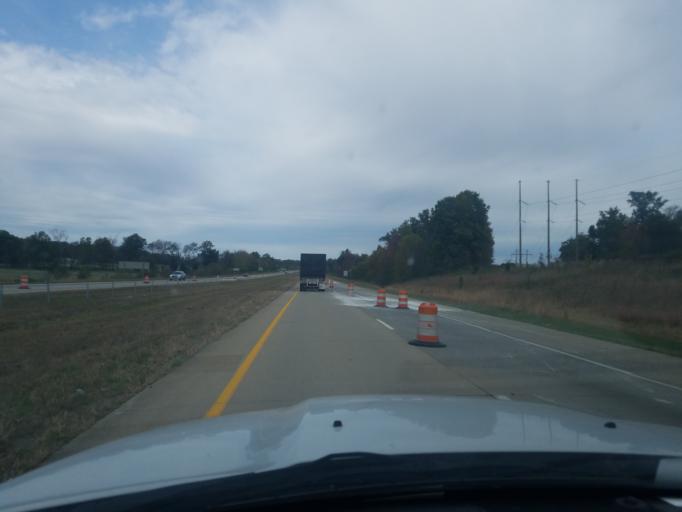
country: US
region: Indiana
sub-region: Gibson County
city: Haubstadt
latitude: 38.1534
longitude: -87.4726
